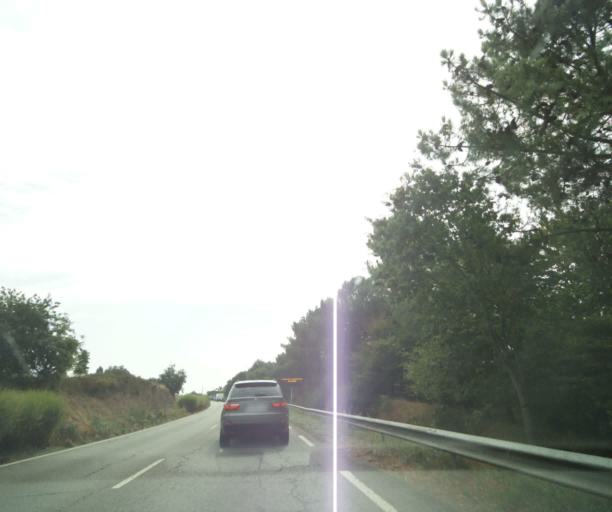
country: FR
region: Pays de la Loire
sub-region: Departement de la Loire-Atlantique
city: Saint-Herblain
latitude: 47.2118
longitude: -1.6316
